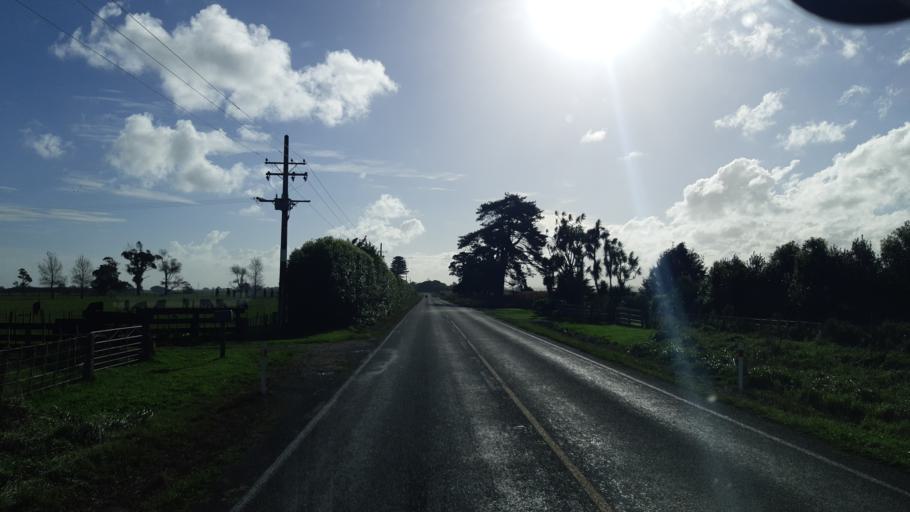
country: NZ
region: Manawatu-Wanganui
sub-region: Wanganui District
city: Wanganui
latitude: -39.9578
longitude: 175.1771
